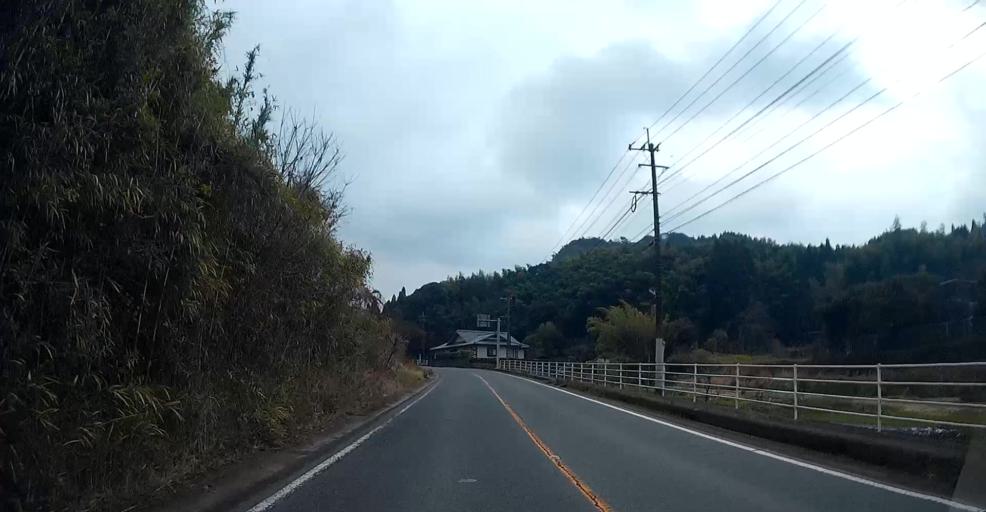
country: JP
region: Kumamoto
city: Matsubase
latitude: 32.6461
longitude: 130.7285
